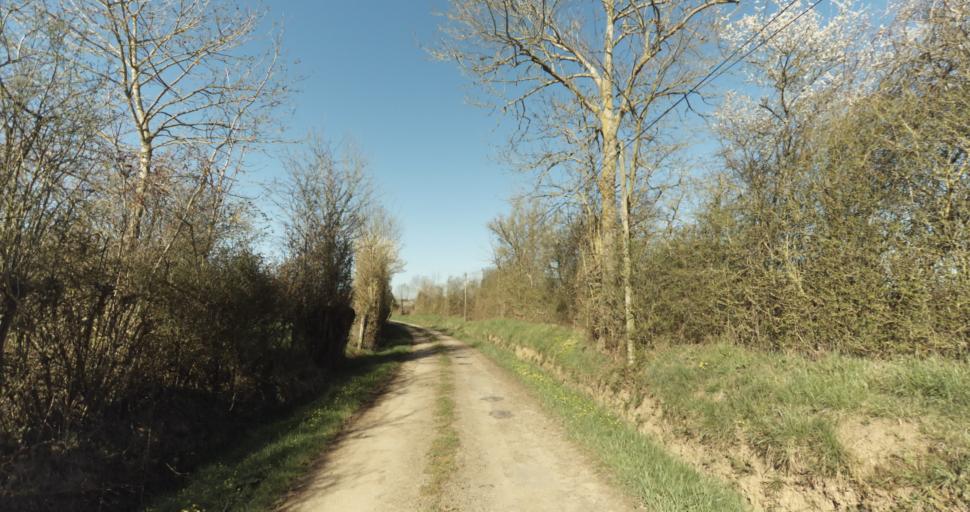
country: FR
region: Lower Normandy
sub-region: Departement du Calvados
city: Saint-Pierre-sur-Dives
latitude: 48.9737
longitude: 0.0013
